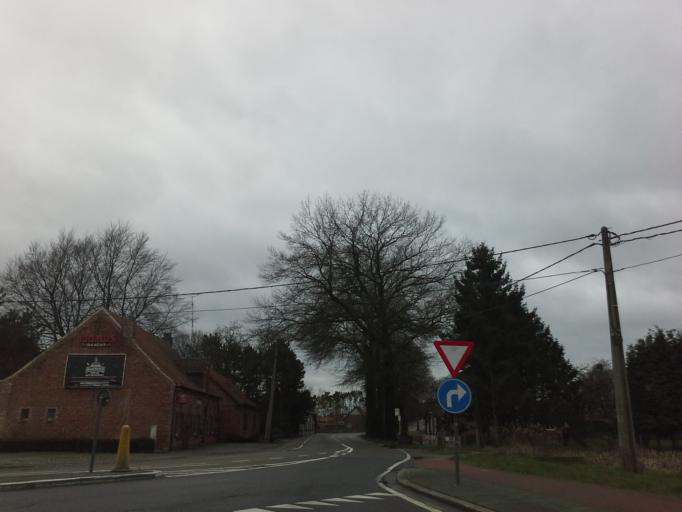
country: BE
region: Flanders
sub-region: Provincie Antwerpen
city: Olen
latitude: 51.1572
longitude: 4.8482
